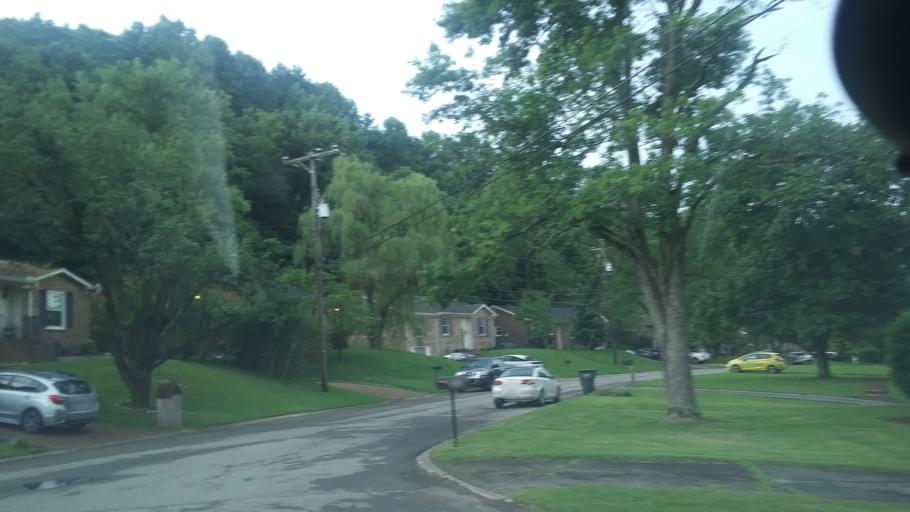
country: US
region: Tennessee
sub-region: Davidson County
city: Belle Meade
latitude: 36.0901
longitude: -86.9305
